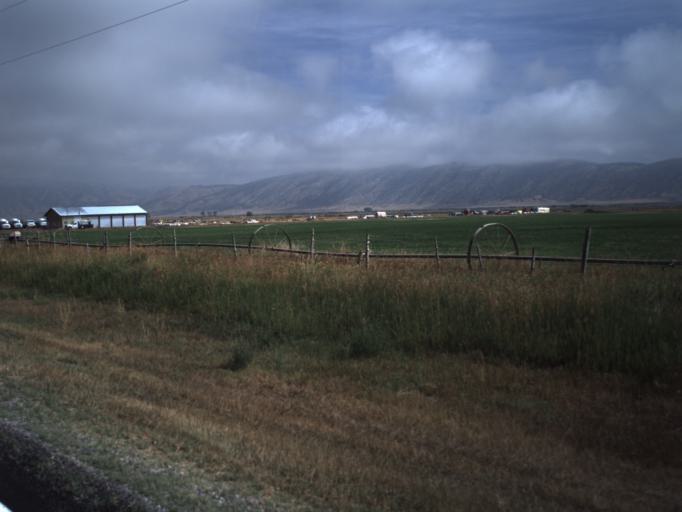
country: US
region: Utah
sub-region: Rich County
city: Randolph
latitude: 41.5280
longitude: -111.1629
